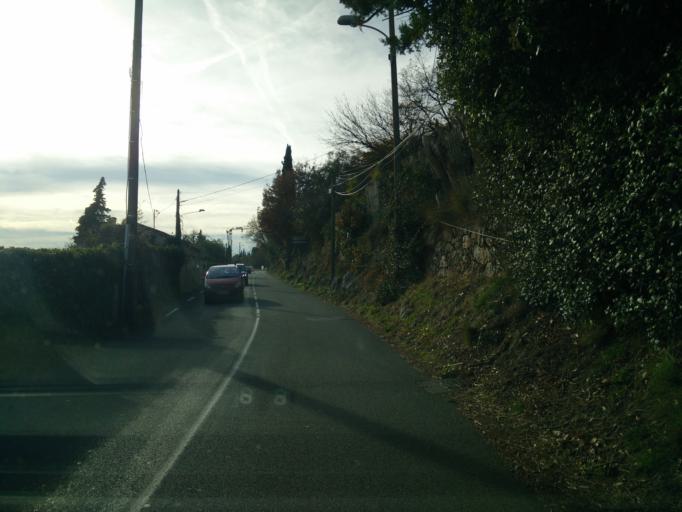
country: FR
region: Provence-Alpes-Cote d'Azur
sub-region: Departement des Alpes-Maritimes
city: Speracedes
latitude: 43.6470
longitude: 6.8565
